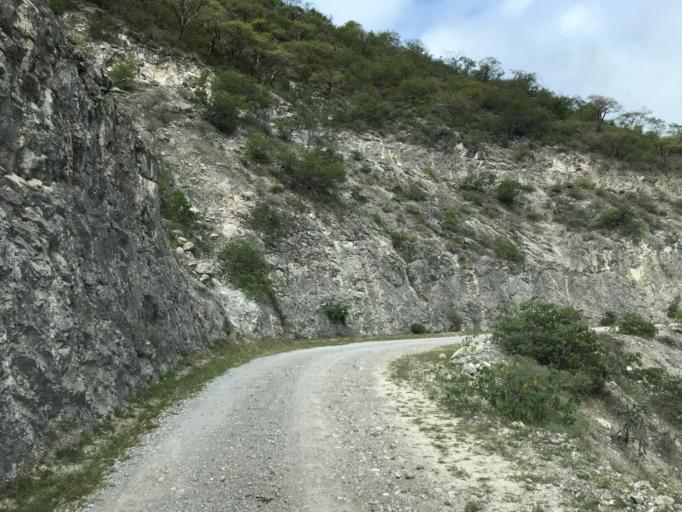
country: MX
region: Hidalgo
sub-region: Metztitlan
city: Fontezuelas
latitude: 20.6420
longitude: -98.9329
